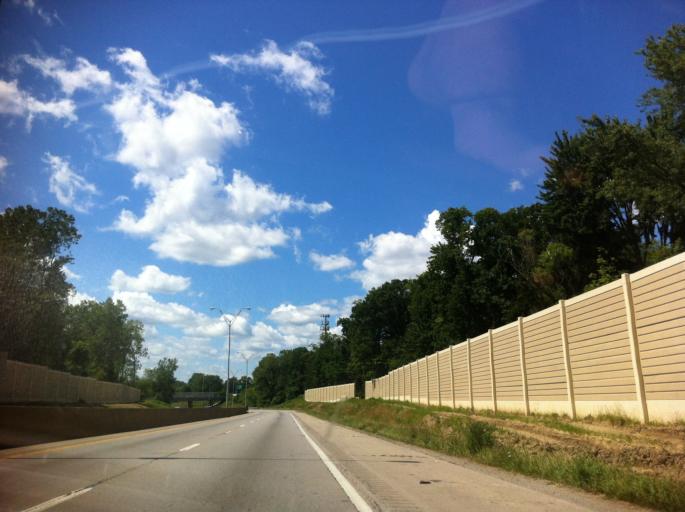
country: US
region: Ohio
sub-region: Lucas County
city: Ottawa Hills
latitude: 41.6890
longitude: -83.6584
